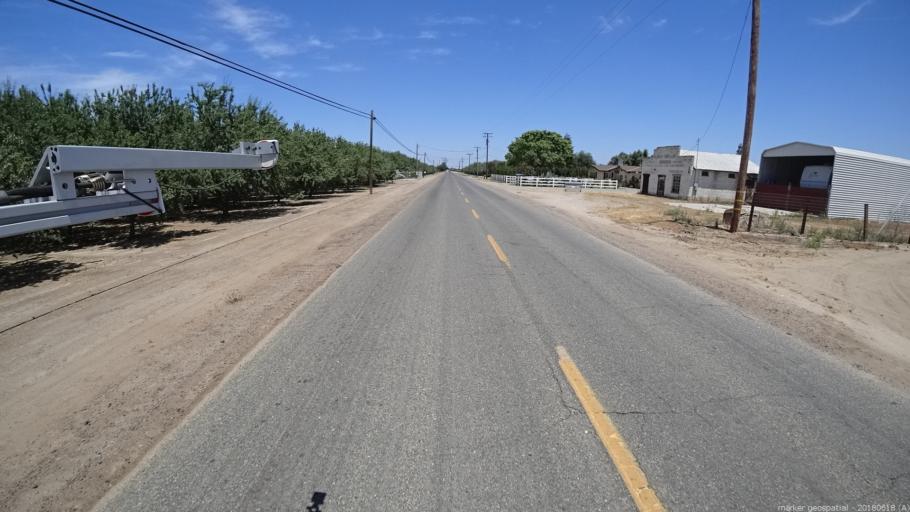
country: US
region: California
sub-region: Madera County
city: Parkwood
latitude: 36.9062
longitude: -120.0924
